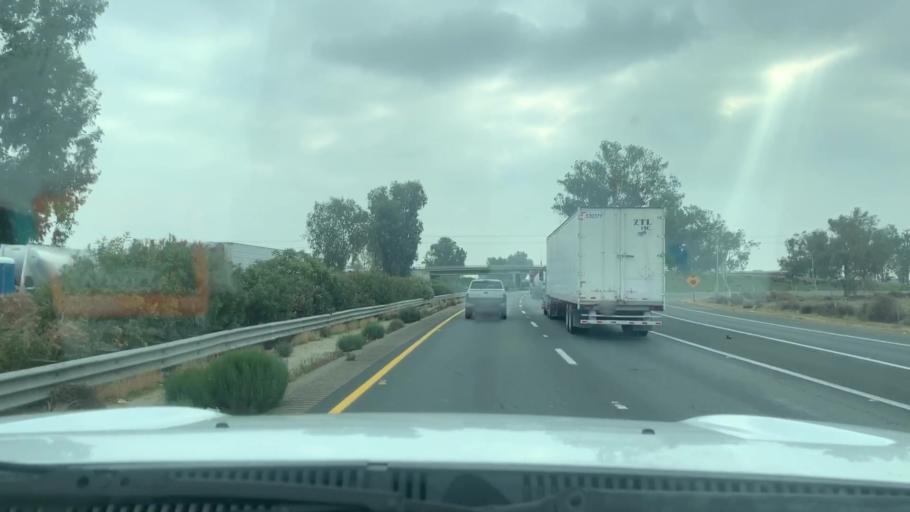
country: US
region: California
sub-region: Tulare County
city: Tipton
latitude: 36.0532
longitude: -119.3110
